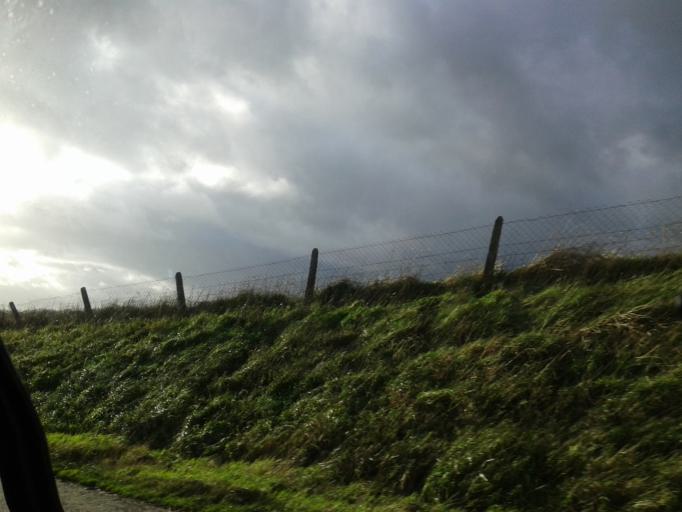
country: IE
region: Leinster
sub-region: An Mhi
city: Slane
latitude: 53.7347
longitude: -6.5132
